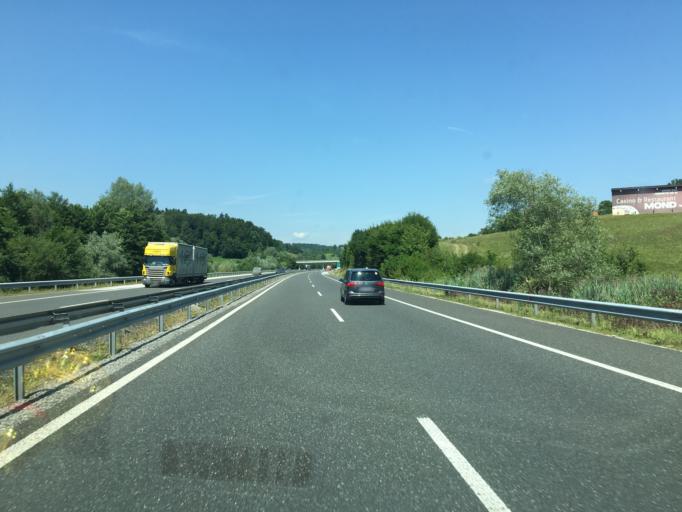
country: SI
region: Kungota
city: Zgornja Kungota
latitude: 46.6397
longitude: 15.6535
